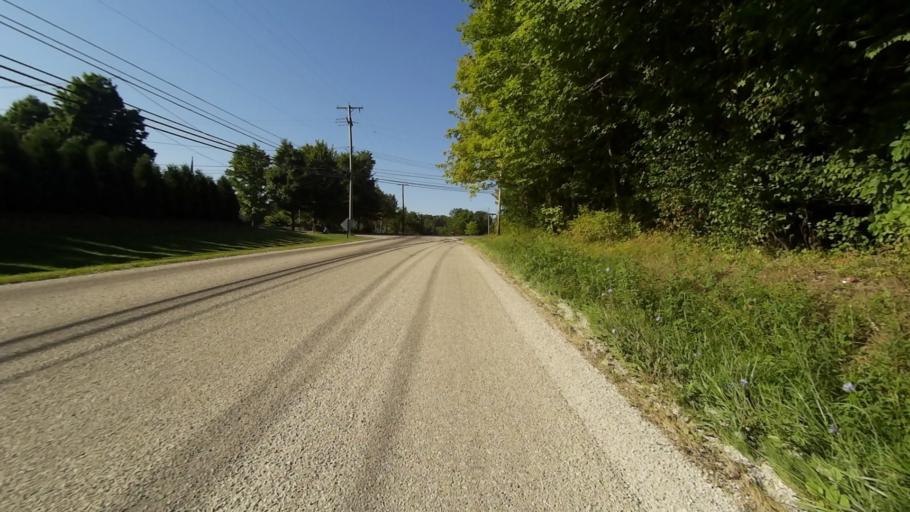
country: US
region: Ohio
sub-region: Portage County
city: Mantua
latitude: 41.2616
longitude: -81.2804
